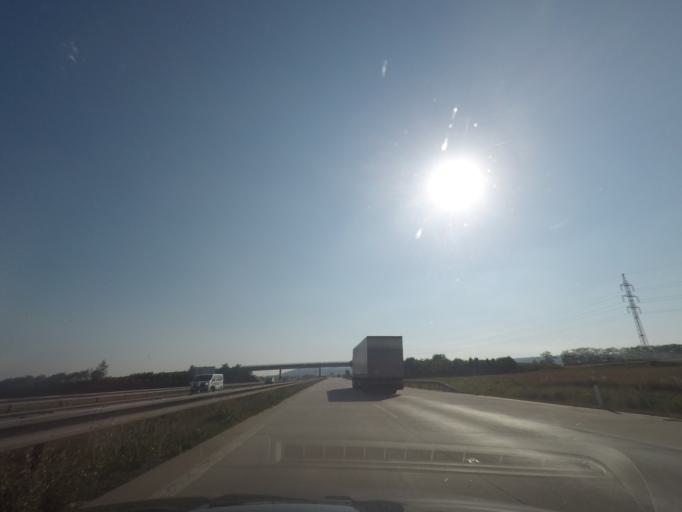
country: CZ
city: Kunin
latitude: 49.6945
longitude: 17.9681
